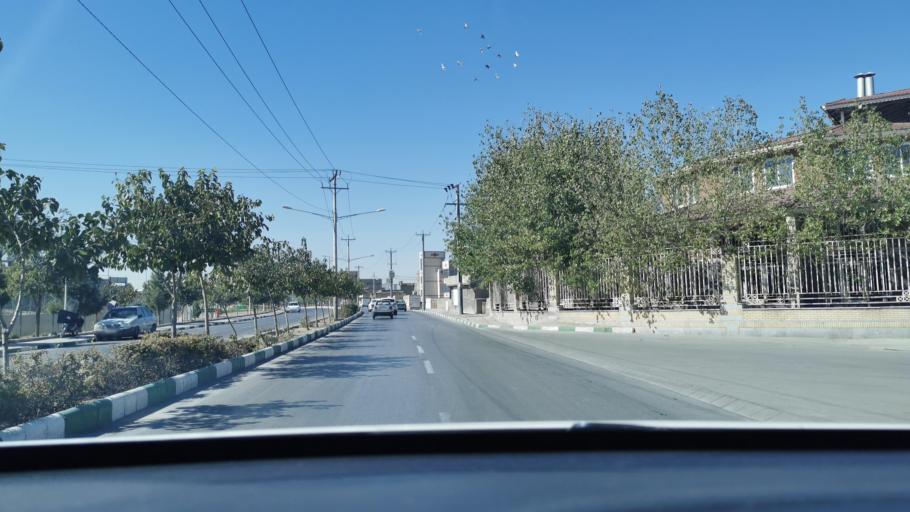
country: IR
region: Razavi Khorasan
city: Mashhad
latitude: 36.3348
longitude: 59.6171
